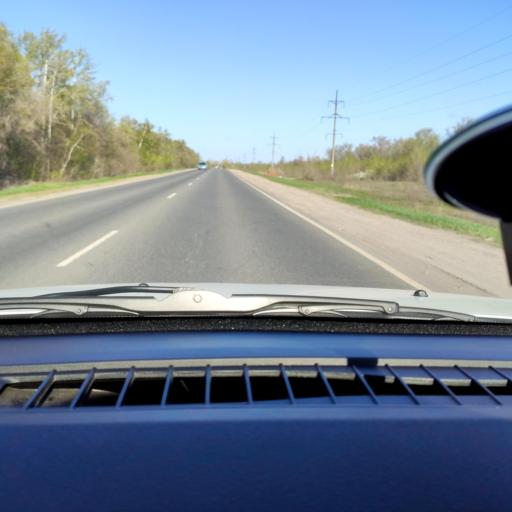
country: RU
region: Samara
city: Dubovyy Umet
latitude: 53.1000
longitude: 50.2602
